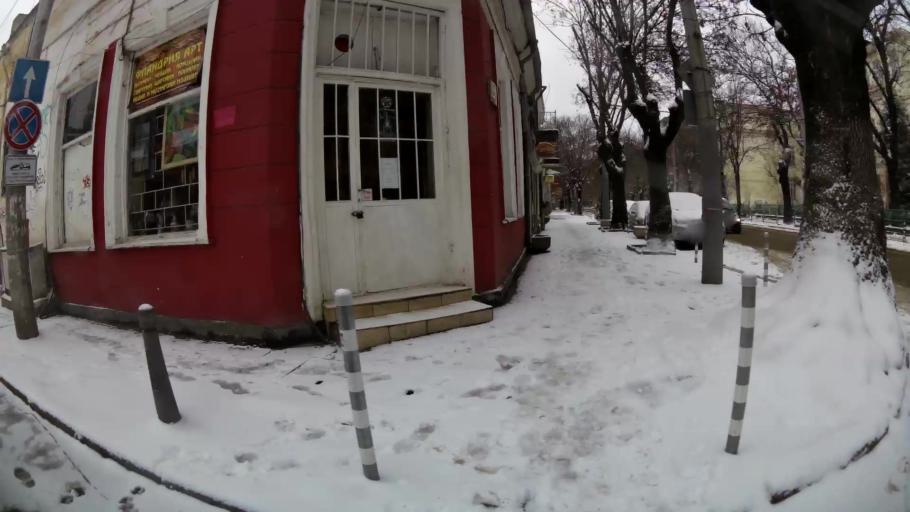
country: BG
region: Sofia-Capital
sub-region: Stolichna Obshtina
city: Sofia
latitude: 42.7008
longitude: 23.3122
